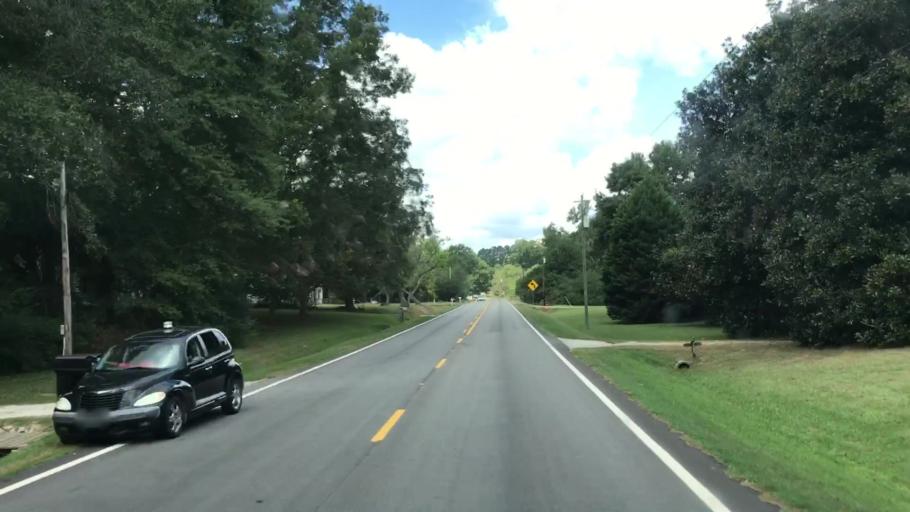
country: US
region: Georgia
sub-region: Greene County
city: Greensboro
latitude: 33.5638
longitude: -83.1445
